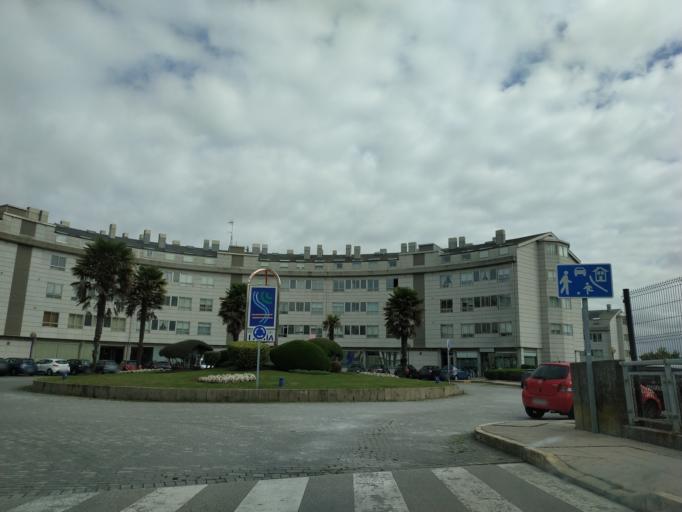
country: ES
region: Galicia
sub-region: Provincia da Coruna
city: Culleredo
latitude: 43.3282
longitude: -8.3812
